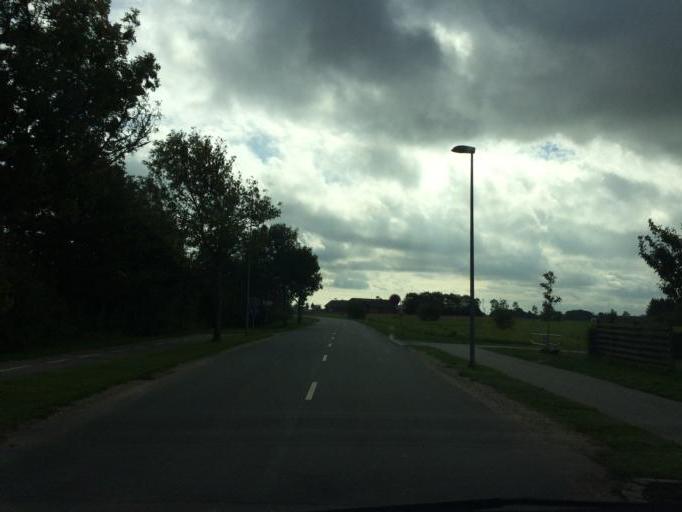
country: DK
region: North Denmark
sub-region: Bronderslev Kommune
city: Dronninglund
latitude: 57.1511
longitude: 10.2819
